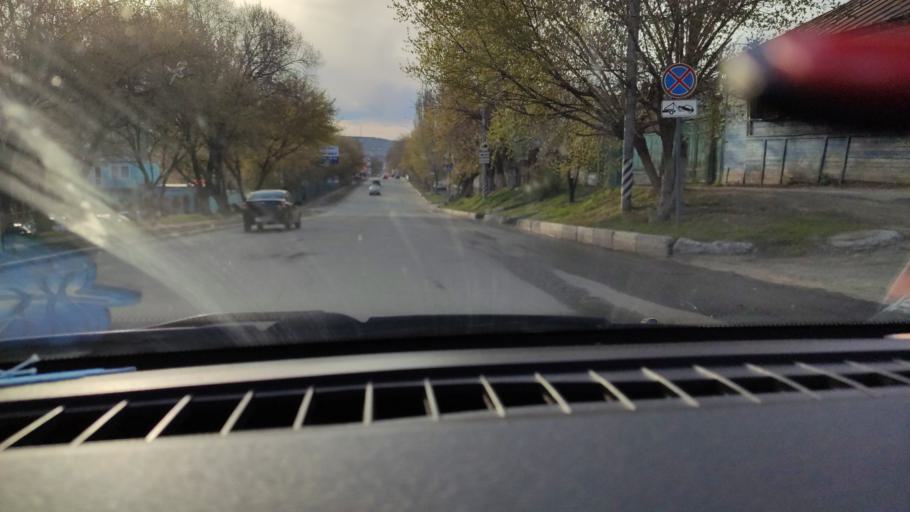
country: RU
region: Saratov
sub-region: Saratovskiy Rayon
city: Saratov
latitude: 51.5418
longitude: 46.0426
